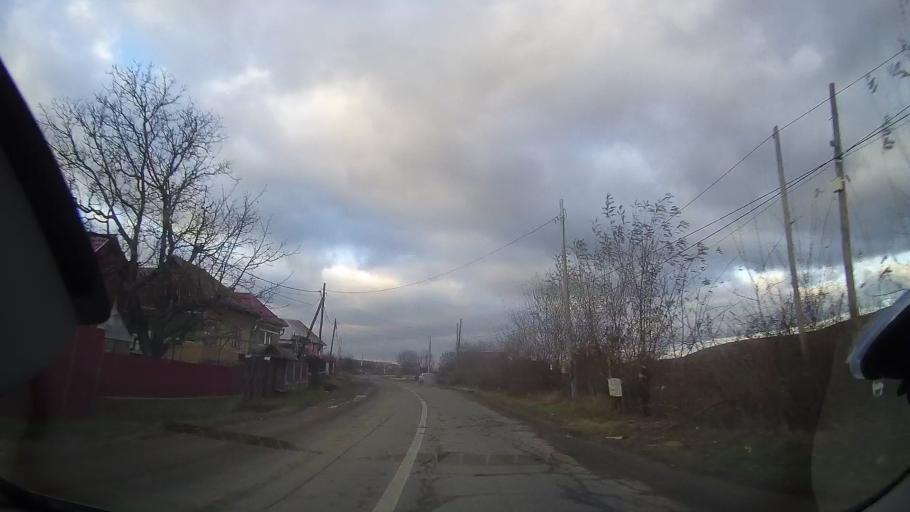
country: RO
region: Cluj
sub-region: Comuna Sancraiu
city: Sancraiu
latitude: 46.8066
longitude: 22.9943
